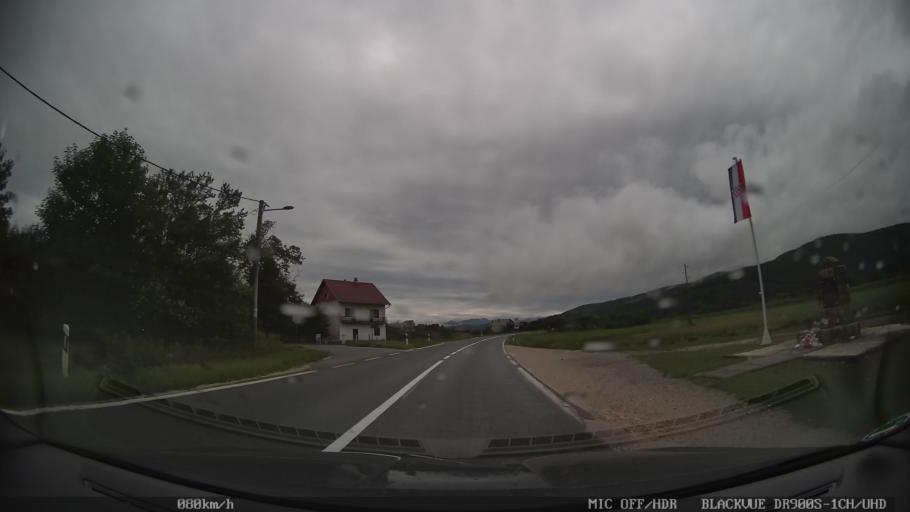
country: HR
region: Licko-Senjska
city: Brinje
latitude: 44.9483
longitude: 15.1256
